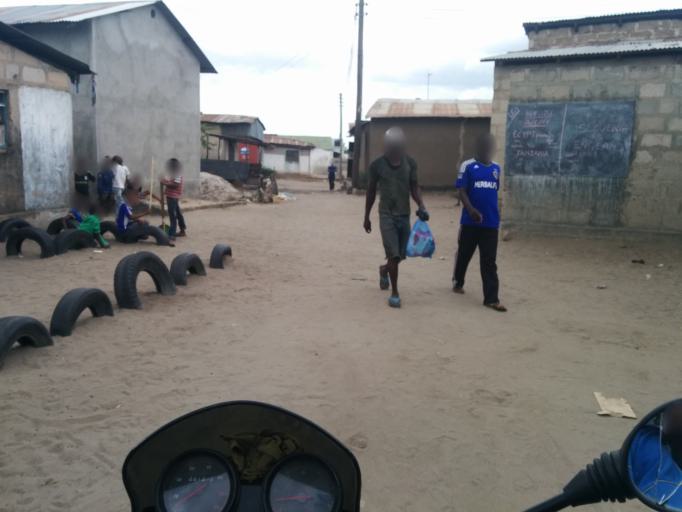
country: TZ
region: Dar es Salaam
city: Dar es Salaam
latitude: -6.8713
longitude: 39.2481
